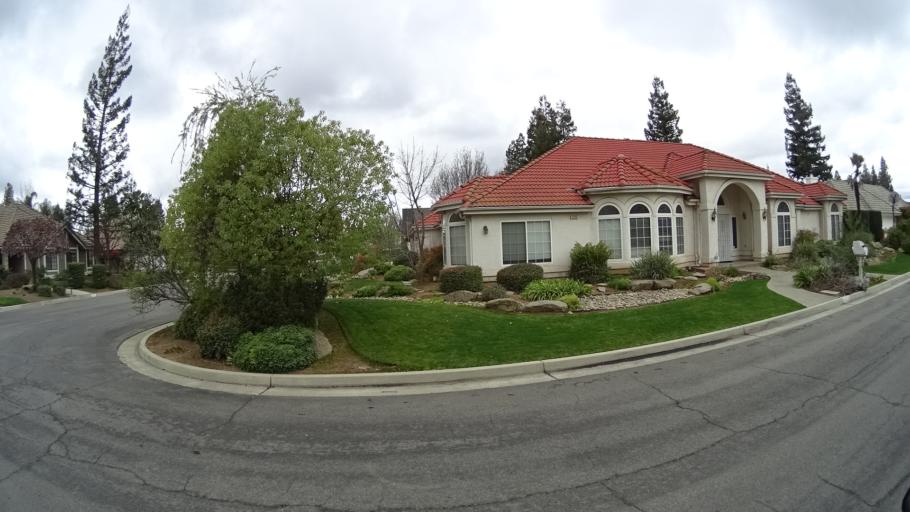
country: US
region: California
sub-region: Fresno County
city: Fresno
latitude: 36.8403
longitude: -119.8235
